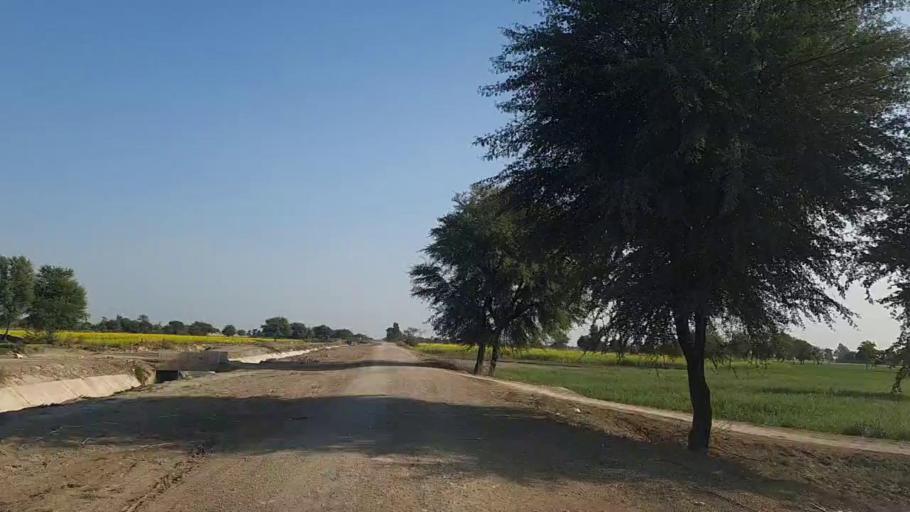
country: PK
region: Sindh
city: Shahpur Chakar
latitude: 26.2031
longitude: 68.6461
